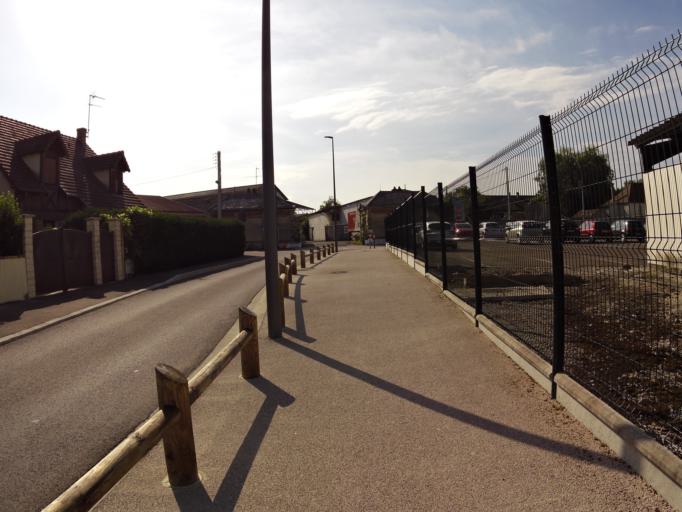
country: FR
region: Champagne-Ardenne
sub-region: Departement de l'Aube
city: Saint-Julien-les-Villas
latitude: 48.2840
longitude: 4.0920
